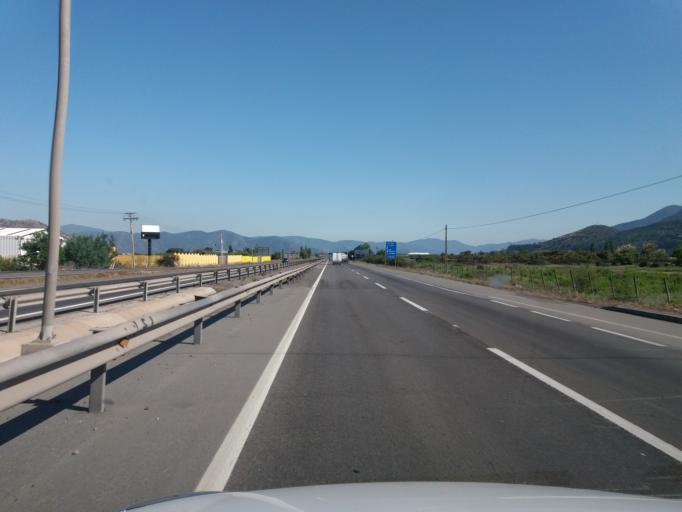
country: CL
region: Valparaiso
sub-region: Provincia de Quillota
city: Hacienda La Calera
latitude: -32.8129
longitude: -71.1456
